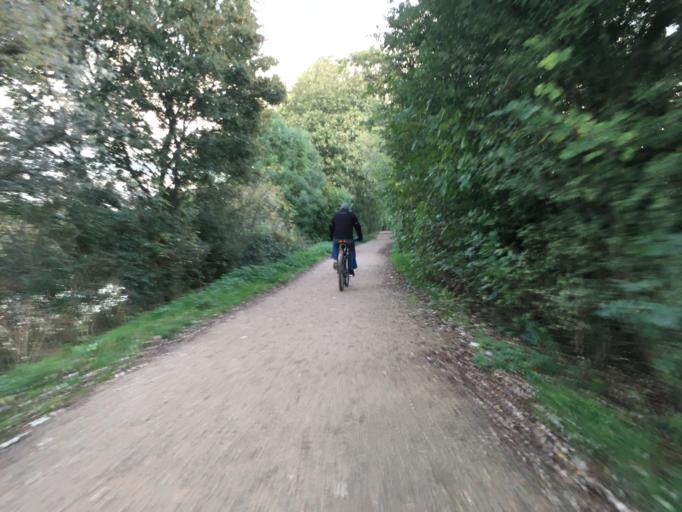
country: DE
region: North Rhine-Westphalia
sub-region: Regierungsbezirk Dusseldorf
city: Oberhausen
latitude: 51.4942
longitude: 6.9005
